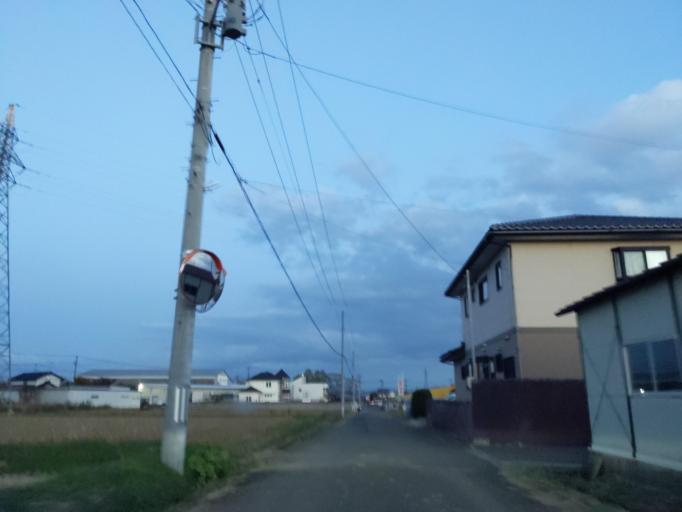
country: JP
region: Fukushima
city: Koriyama
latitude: 37.4614
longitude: 140.3266
